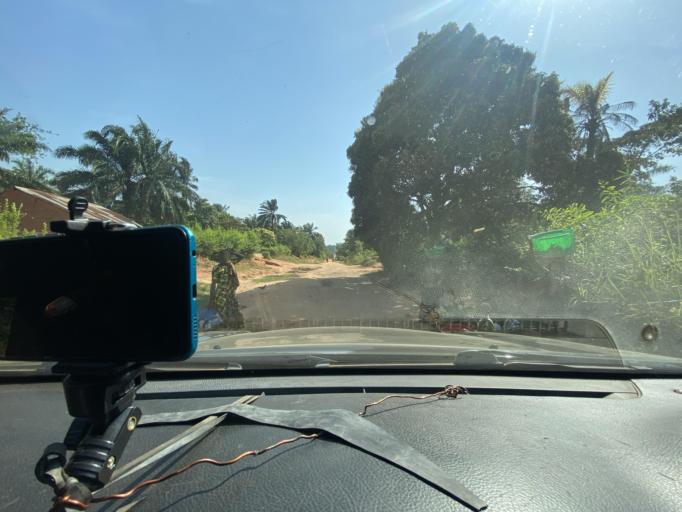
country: CD
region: Kasai-Oriental
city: Kabinda
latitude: -6.1206
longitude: 24.5272
